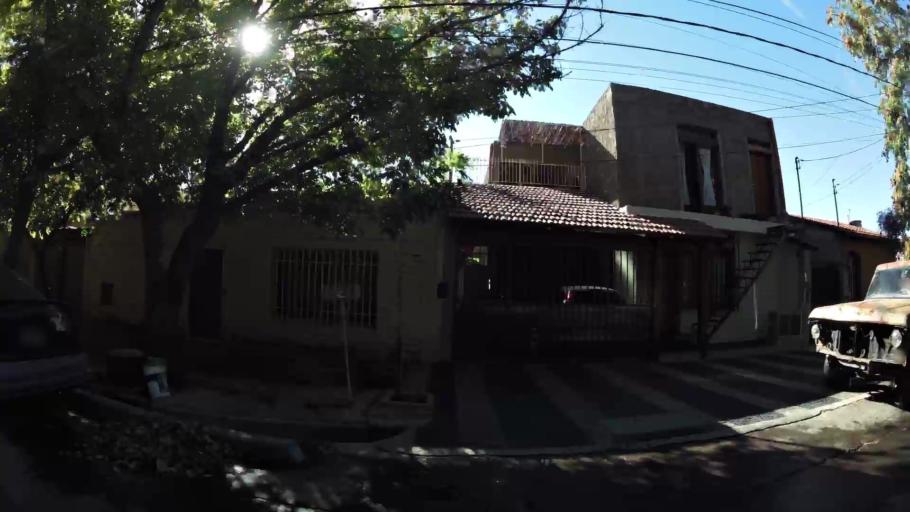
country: AR
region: Mendoza
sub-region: Departamento de Godoy Cruz
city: Godoy Cruz
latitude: -32.9218
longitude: -68.8551
